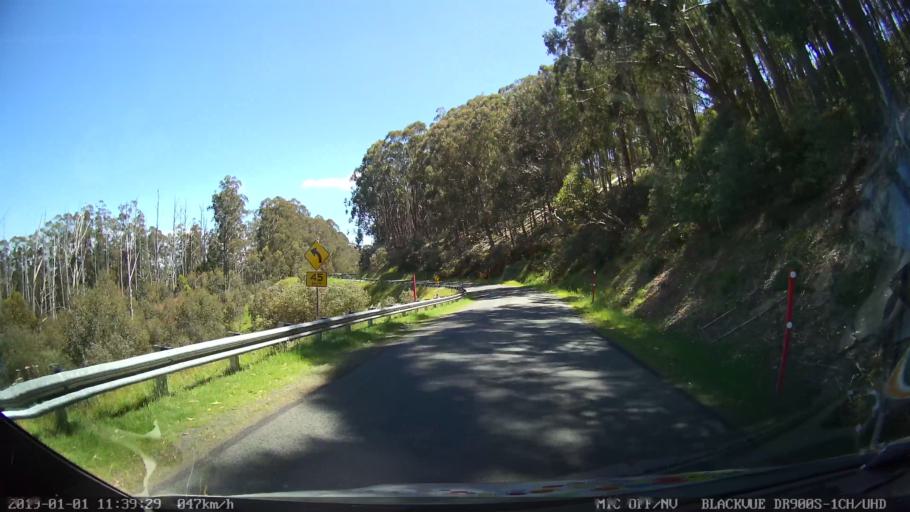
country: AU
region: New South Wales
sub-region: Snowy River
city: Jindabyne
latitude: -35.9263
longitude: 148.3863
